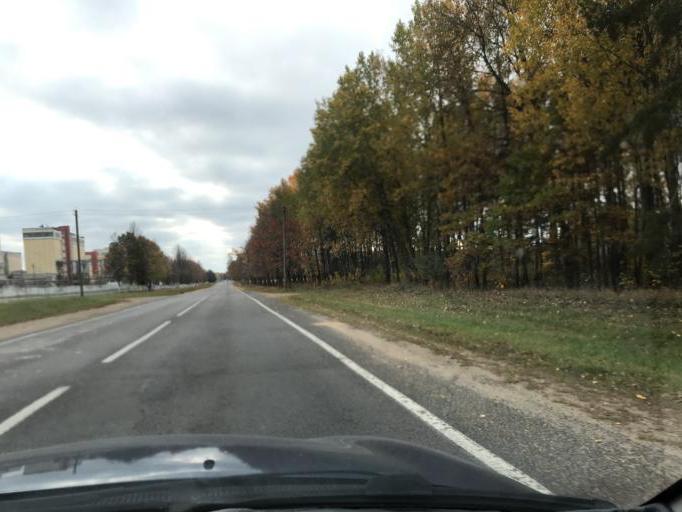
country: BY
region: Grodnenskaya
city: Lida
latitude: 53.9459
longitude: 25.2460
